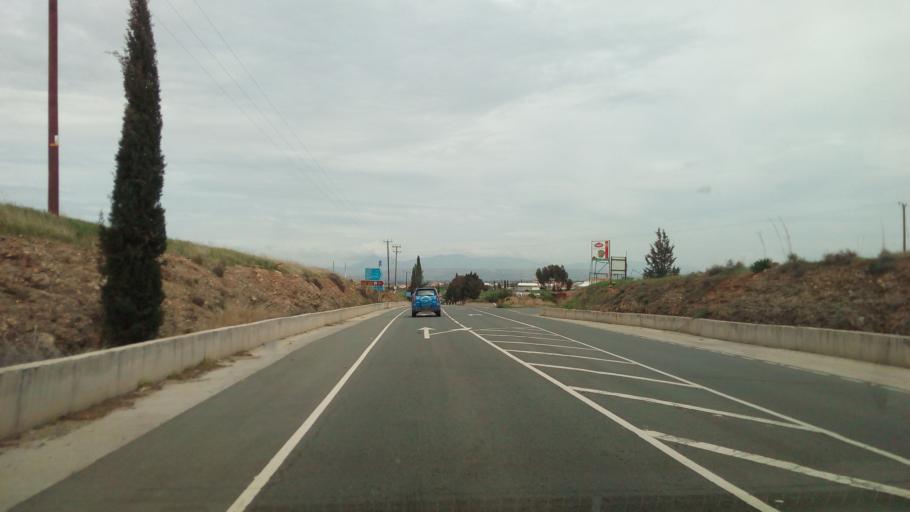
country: CY
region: Lefkosia
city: Astromeritis
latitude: 35.1266
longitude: 33.0123
